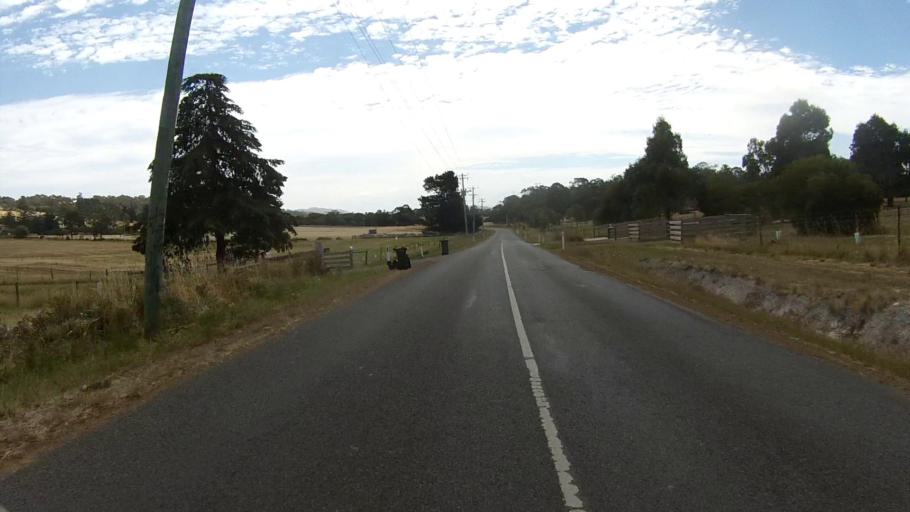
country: AU
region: Tasmania
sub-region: Clarence
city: Sandford
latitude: -42.9821
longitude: 147.5135
